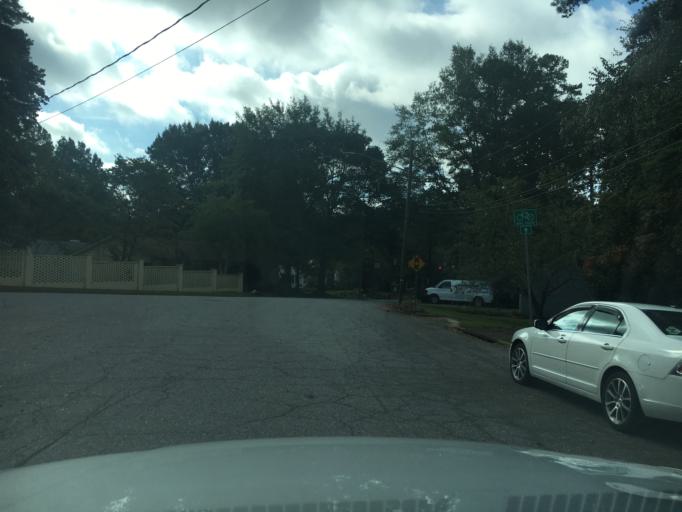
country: US
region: North Carolina
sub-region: Catawba County
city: Hickory
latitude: 35.7439
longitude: -81.3377
